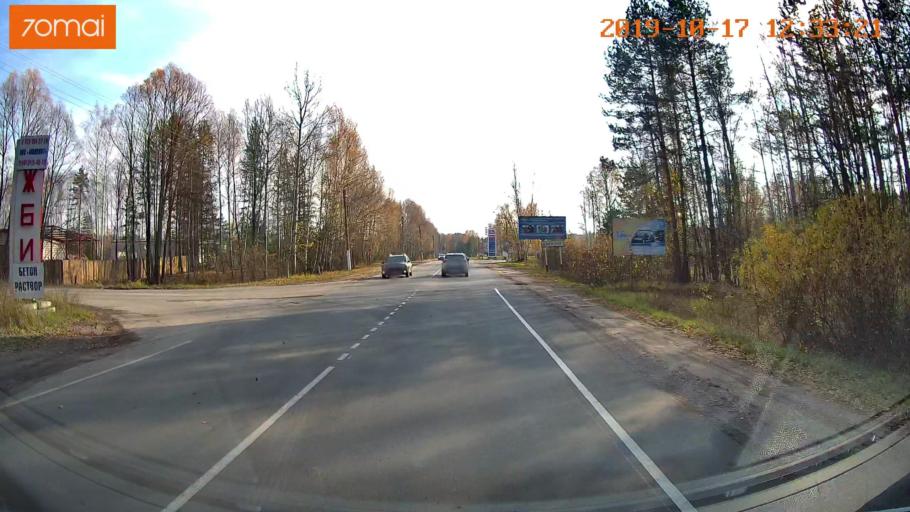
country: RU
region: Rjazan
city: Kasimov
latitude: 54.9553
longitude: 41.3531
